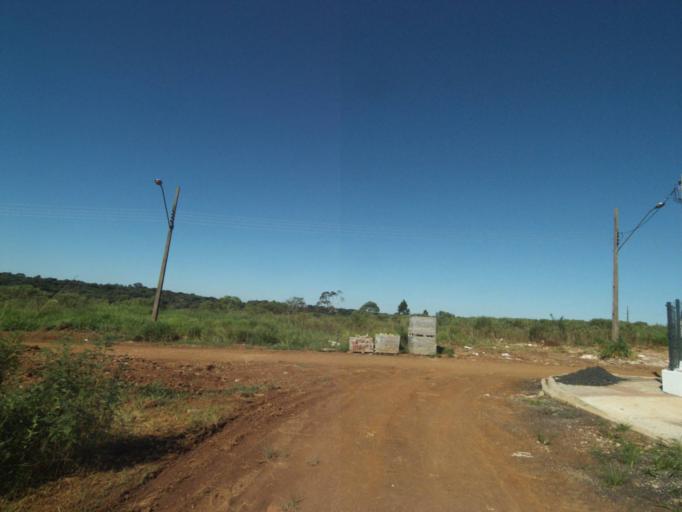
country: BR
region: Parana
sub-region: Pinhao
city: Pinhao
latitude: -25.8365
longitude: -52.0317
